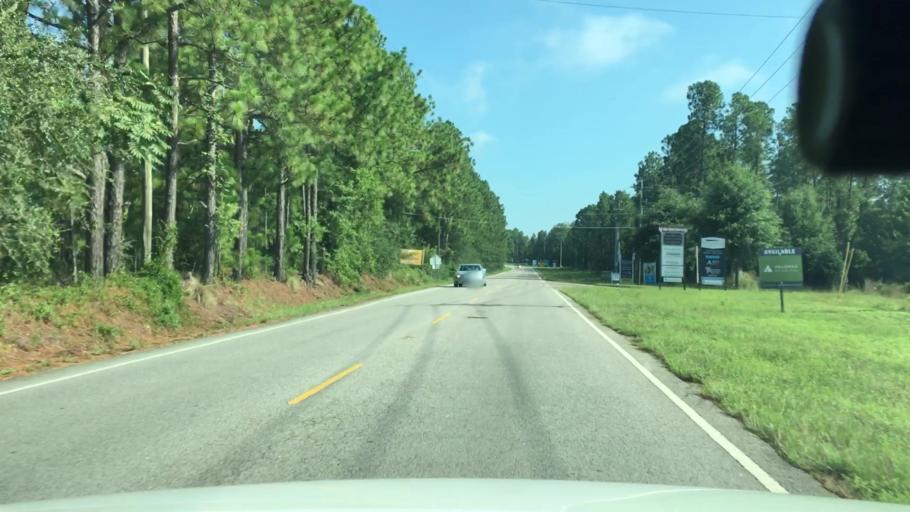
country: US
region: South Carolina
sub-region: Aiken County
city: Graniteville
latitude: 33.5881
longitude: -81.8364
